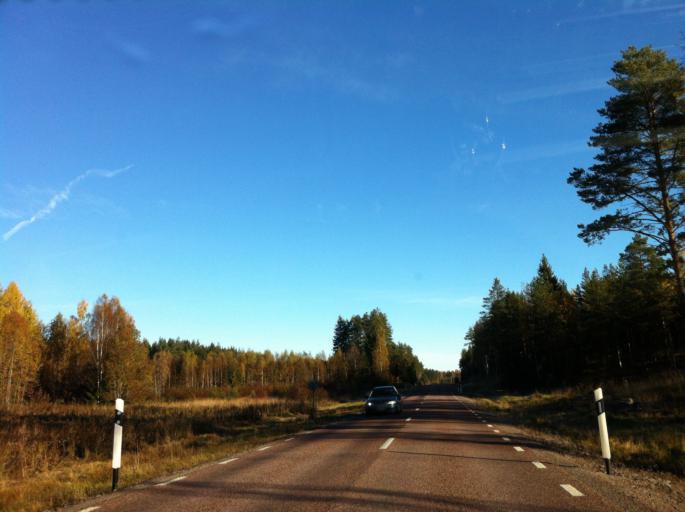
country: SE
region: Gaevleborg
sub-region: Gavle Kommun
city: Gavle
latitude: 60.5600
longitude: 17.1238
